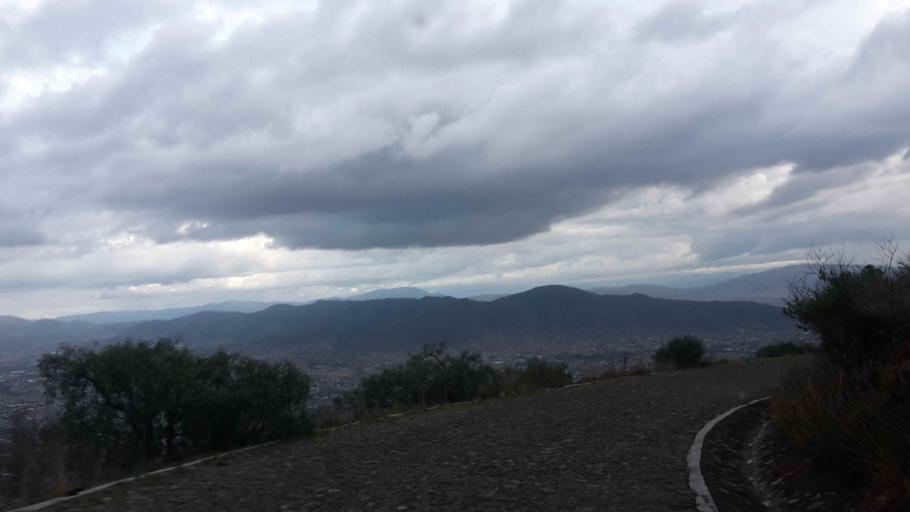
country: BO
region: Cochabamba
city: Cochabamba
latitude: -17.3649
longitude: -66.0638
